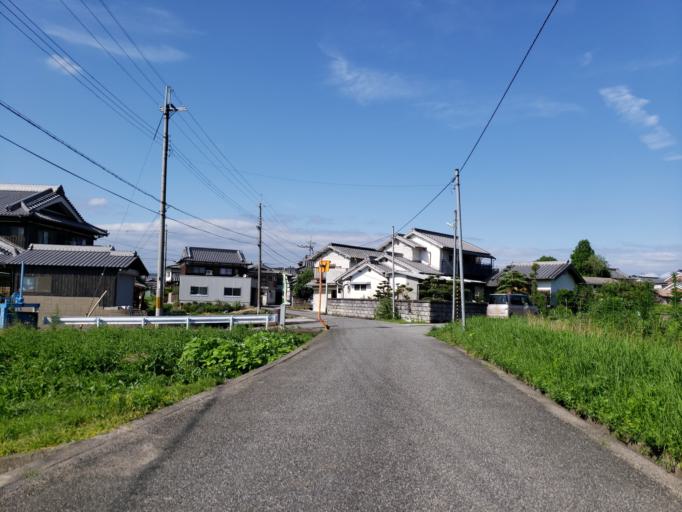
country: JP
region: Hyogo
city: Himeji
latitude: 34.9074
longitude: 134.7724
